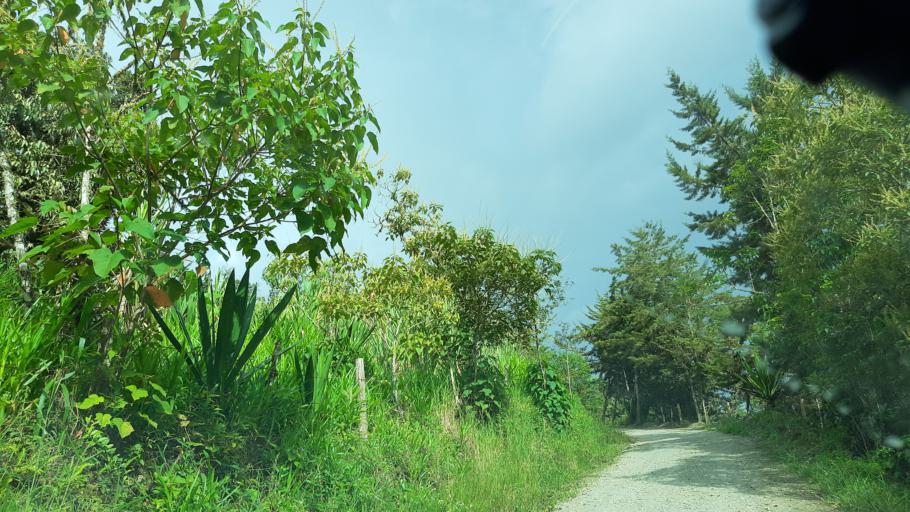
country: CO
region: Boyaca
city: Garagoa
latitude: 5.0377
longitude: -73.3481
